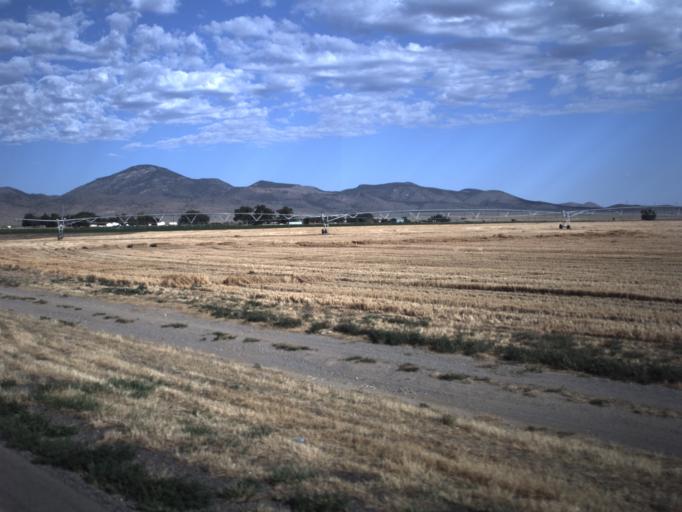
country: US
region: Utah
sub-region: Utah County
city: Genola
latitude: 39.9522
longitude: -111.9432
